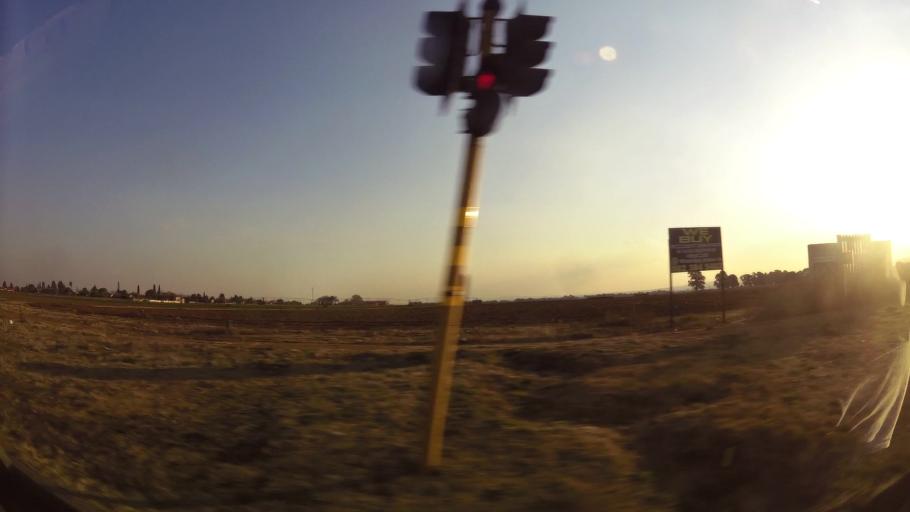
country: ZA
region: Gauteng
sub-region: Ekurhuleni Metropolitan Municipality
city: Boksburg
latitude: -26.2913
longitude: 28.2504
